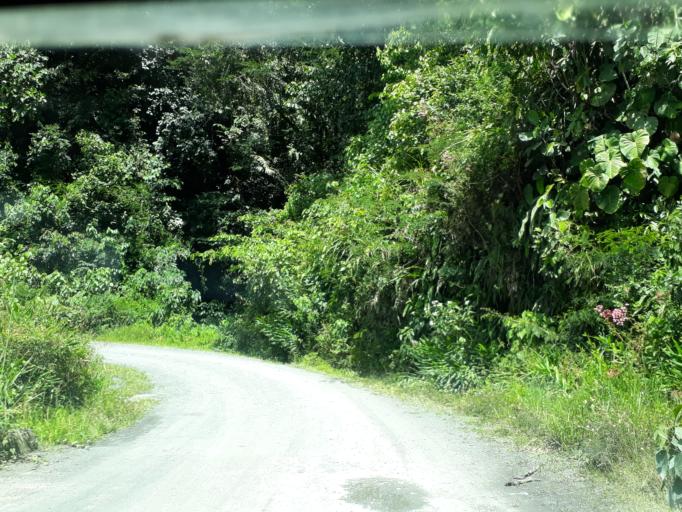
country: CO
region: Cundinamarca
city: Topaipi
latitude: 5.3451
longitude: -74.1987
